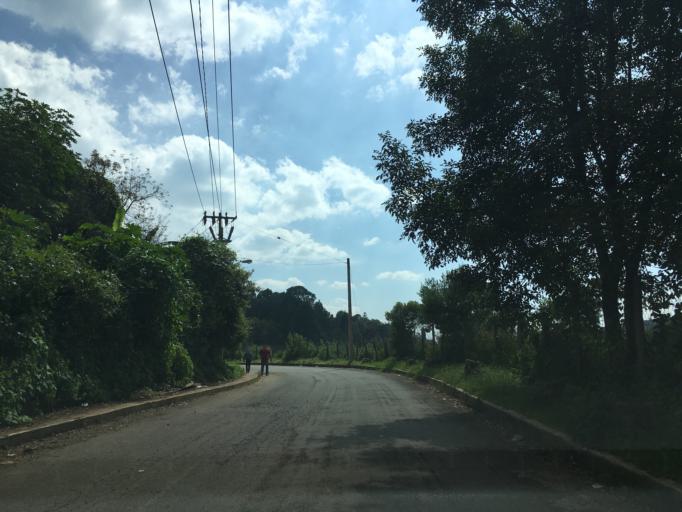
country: MX
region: Michoacan
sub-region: Morelia
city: Montana Monarca (Punta Altozano)
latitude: 19.5805
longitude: -101.1892
